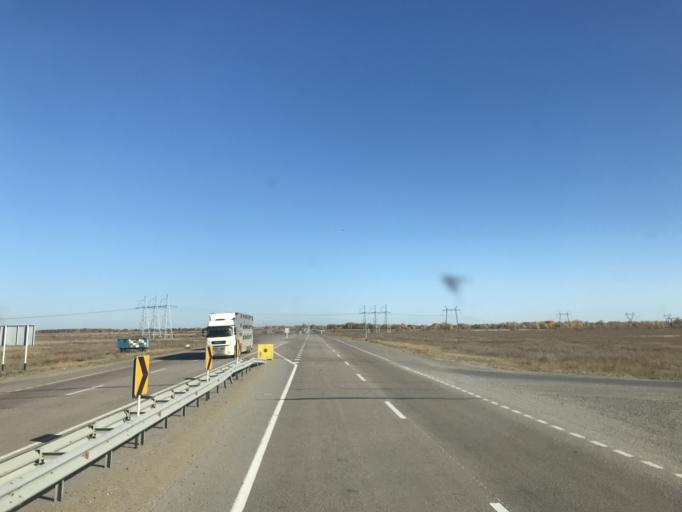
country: KZ
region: Pavlodar
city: Aksu
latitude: 52.1572
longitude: 76.8483
